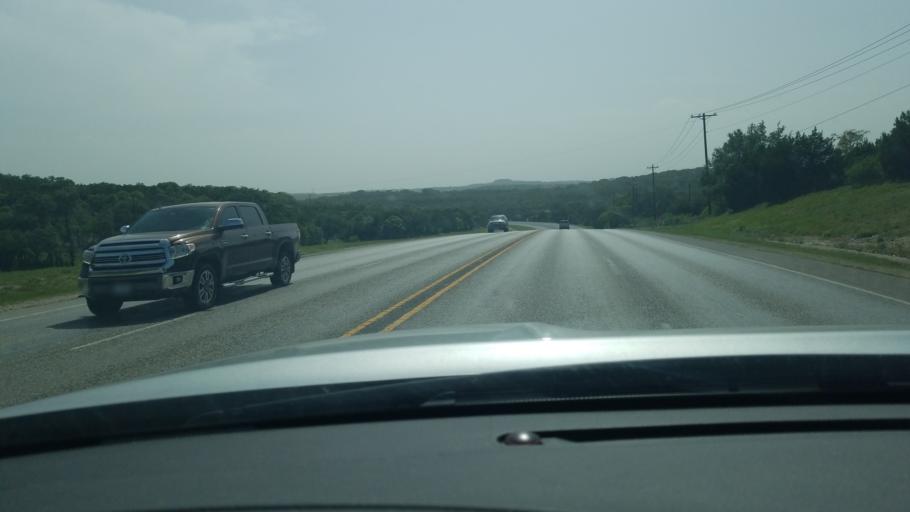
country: US
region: Texas
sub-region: Comal County
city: Bulverde
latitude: 29.7969
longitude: -98.4560
